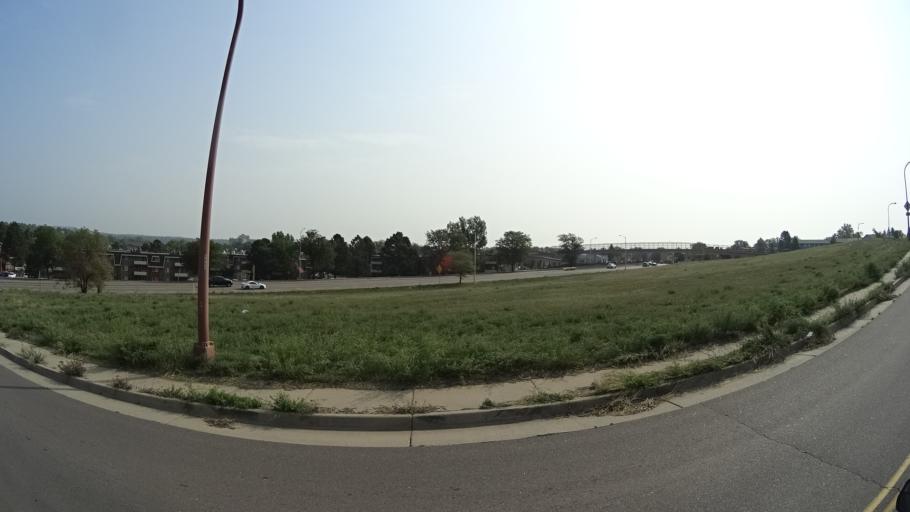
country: US
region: Colorado
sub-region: El Paso County
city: Stratmoor
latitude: 38.8160
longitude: -104.7720
